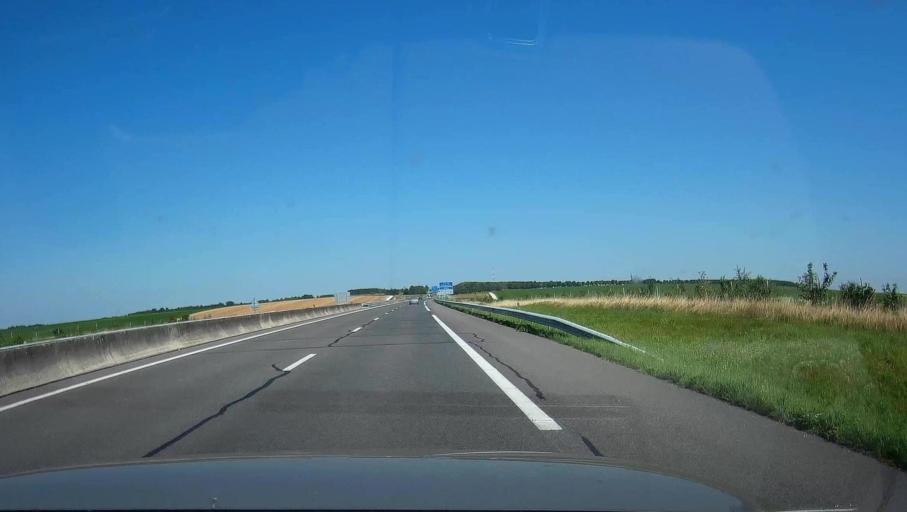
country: FR
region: Champagne-Ardenne
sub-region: Departement de l'Aube
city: Mailly-le-Camp
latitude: 48.7207
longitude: 4.2168
